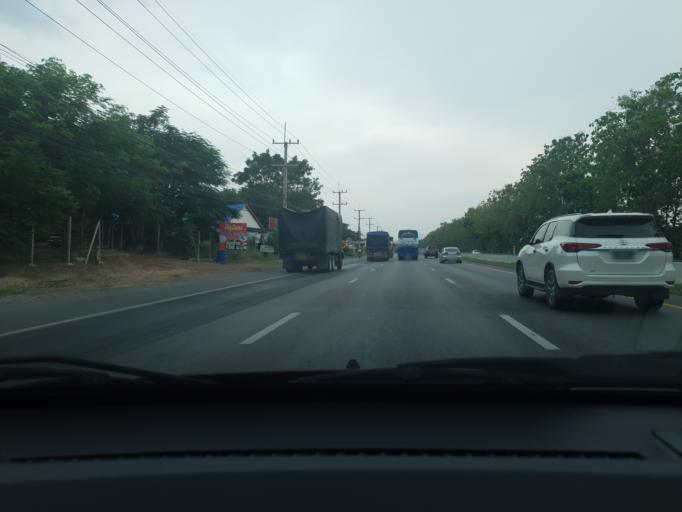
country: TH
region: Phetchaburi
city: Khao Yoi
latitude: 13.2156
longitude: 99.8264
